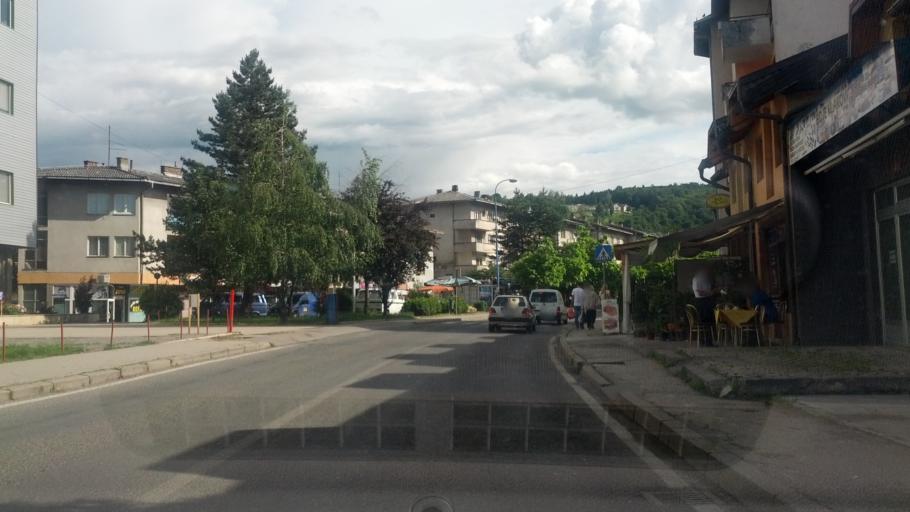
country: BA
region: Federation of Bosnia and Herzegovina
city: Bosanska Krupa
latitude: 44.8835
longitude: 16.1541
